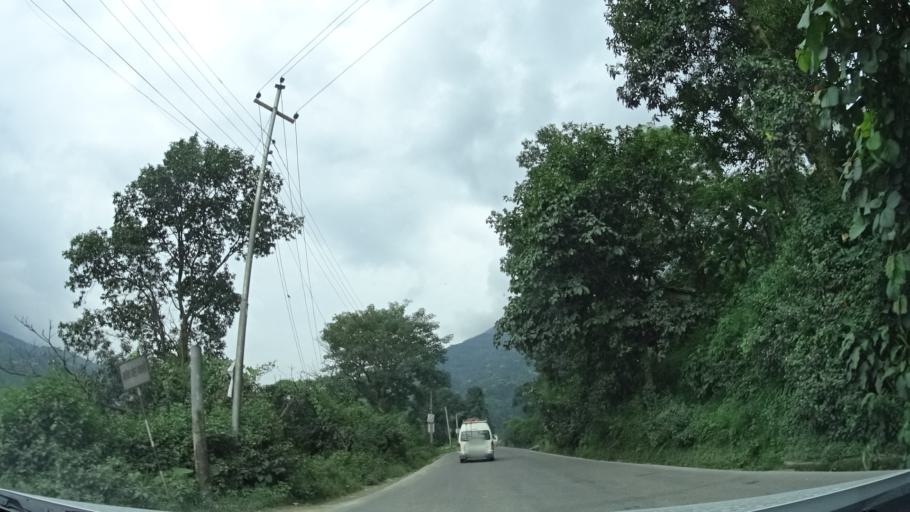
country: NP
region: Central Region
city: Kirtipur
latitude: 27.7179
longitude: 85.1763
